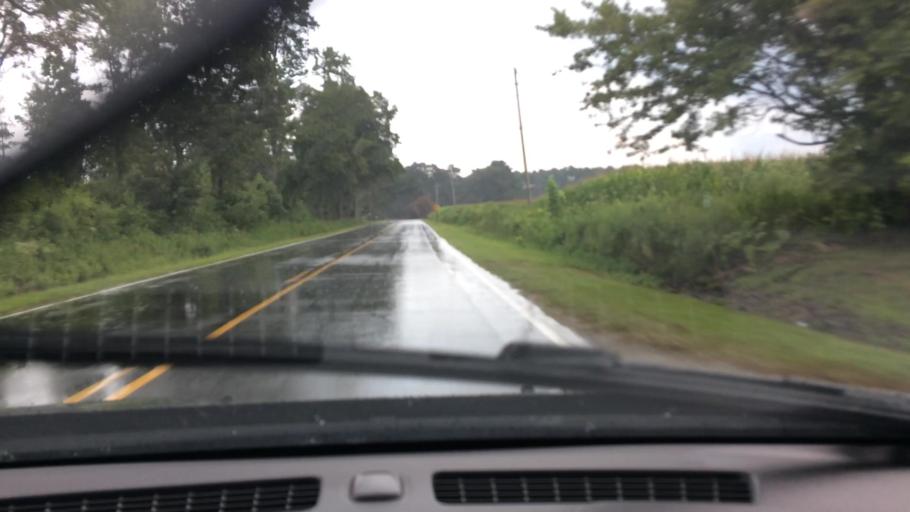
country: US
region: North Carolina
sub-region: Pitt County
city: Winterville
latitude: 35.5090
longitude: -77.3813
